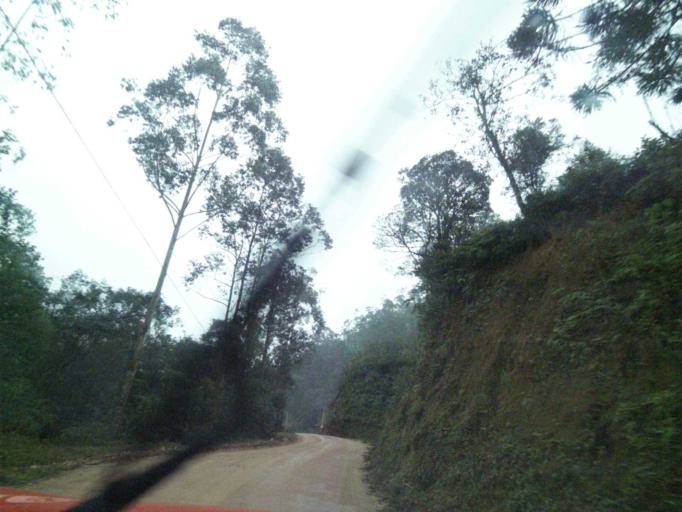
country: BR
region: Santa Catarina
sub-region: Anitapolis
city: Anitapolis
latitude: -27.9209
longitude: -49.1325
